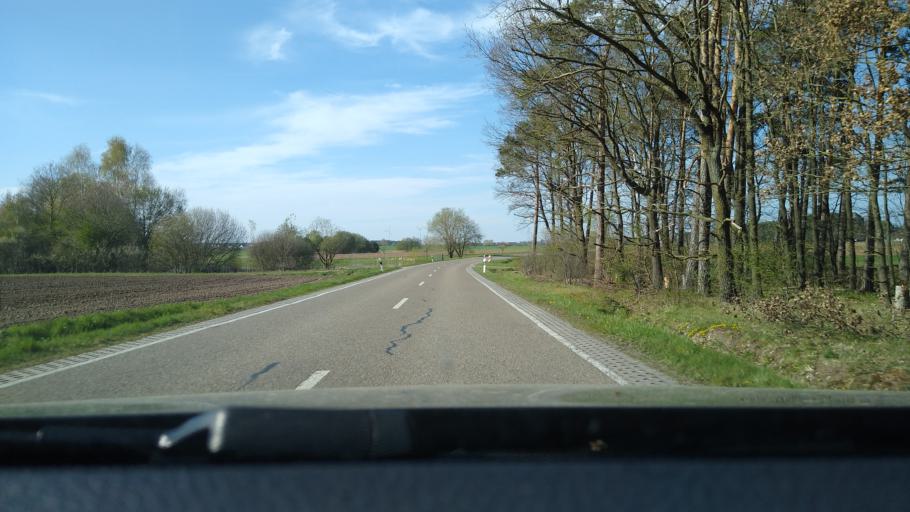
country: DE
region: Bavaria
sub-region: Regierungsbezirk Mittelfranken
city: Merkendorf
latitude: 49.1888
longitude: 10.7229
